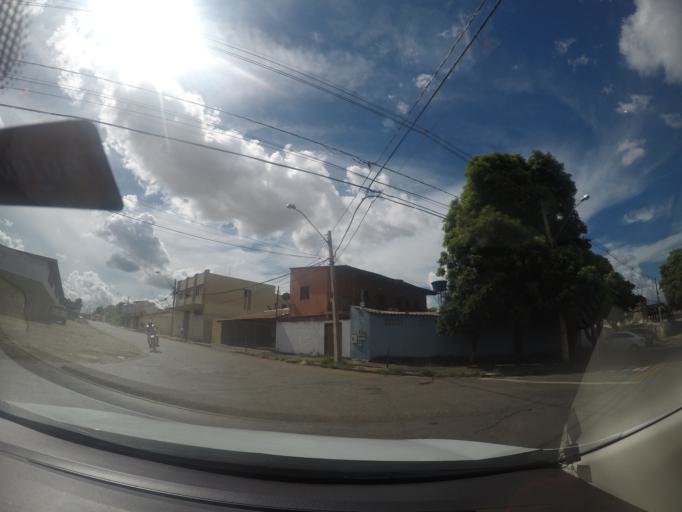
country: BR
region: Goias
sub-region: Goiania
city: Goiania
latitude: -16.6749
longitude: -49.3017
